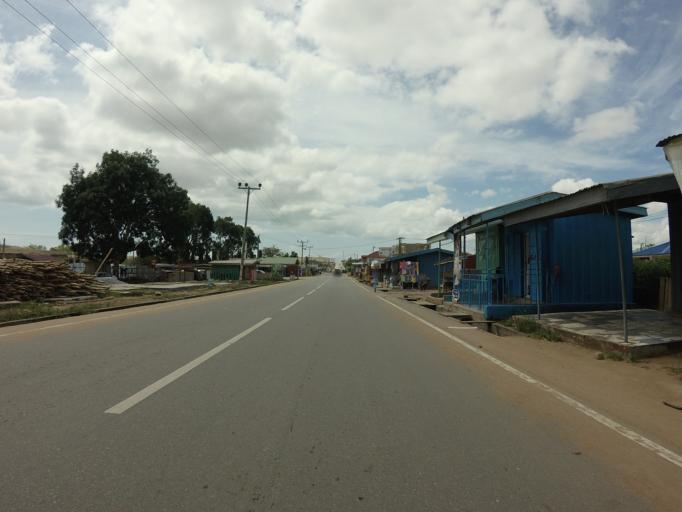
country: GH
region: Central
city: Kasoa
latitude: 5.5357
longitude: -0.4008
